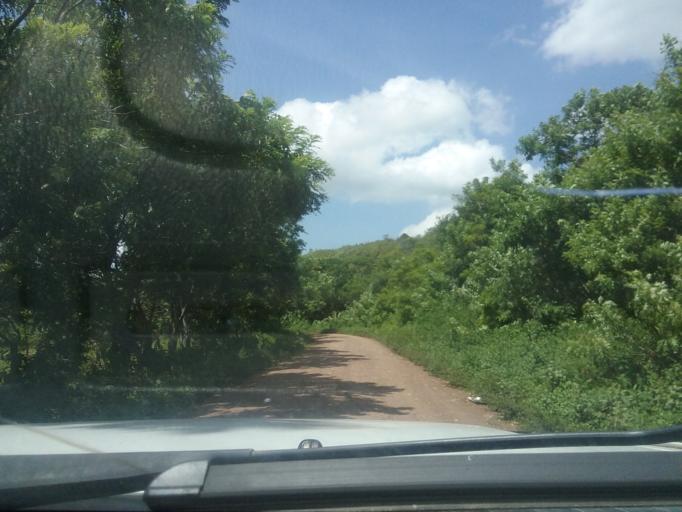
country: NI
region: Matagalpa
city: Terrabona
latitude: 12.6906
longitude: -85.9548
